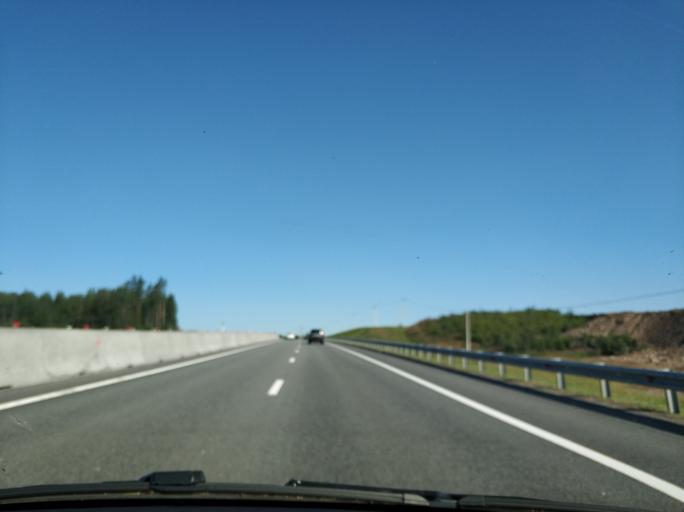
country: RU
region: Leningrad
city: Sosnovo
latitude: 60.5116
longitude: 30.1879
